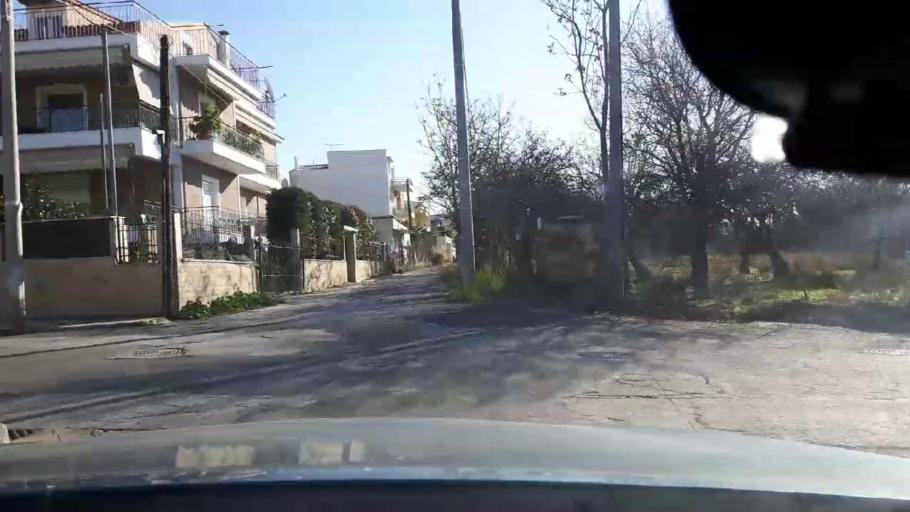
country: GR
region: Attica
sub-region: Nomarchia Athinas
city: Melissia
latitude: 38.0490
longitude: 23.8266
